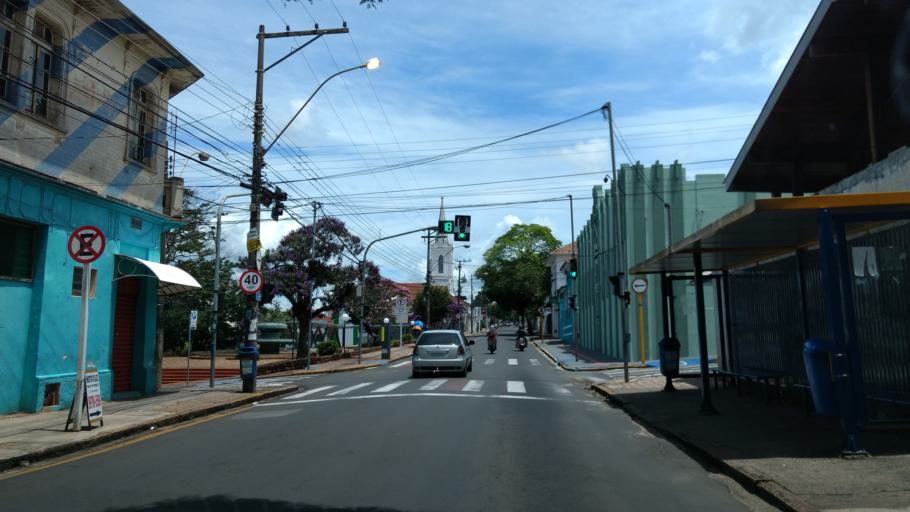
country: BR
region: Sao Paulo
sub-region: Botucatu
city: Botucatu
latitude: -22.8871
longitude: -48.4418
